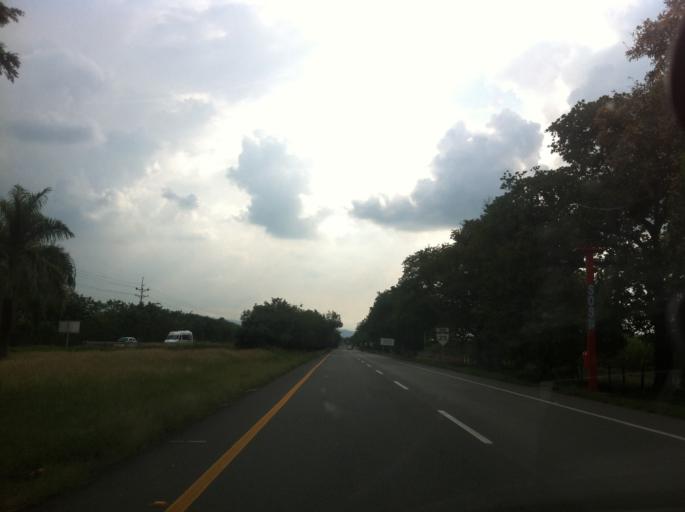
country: CO
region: Valle del Cauca
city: Tulua
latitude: 4.0524
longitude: -76.2034
